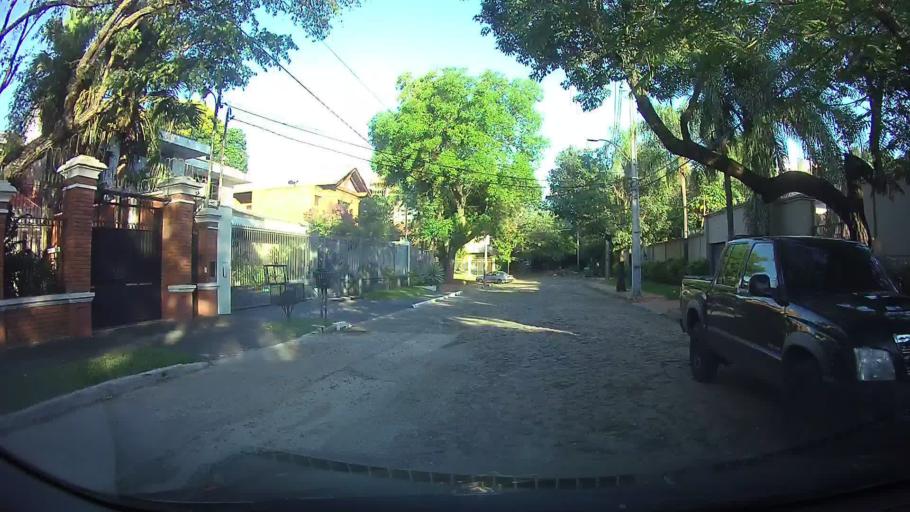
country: PY
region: Asuncion
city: Asuncion
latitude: -25.2832
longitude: -57.5822
